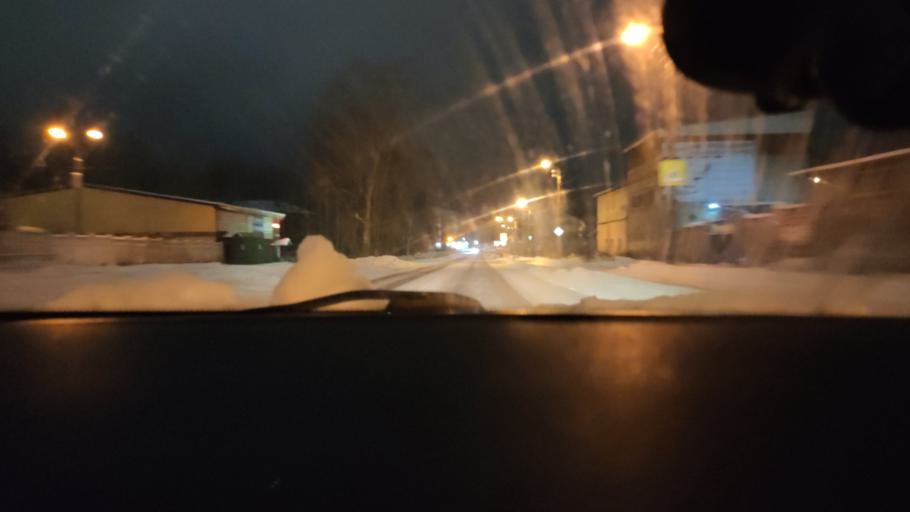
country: RU
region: Perm
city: Krasnokamsk
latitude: 58.0839
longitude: 55.7671
